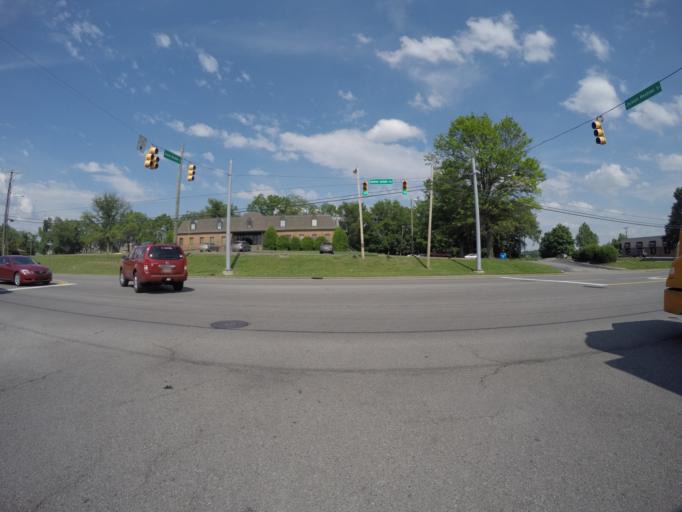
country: US
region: Tennessee
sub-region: Davidson County
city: Lakewood
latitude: 36.2178
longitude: -86.5978
